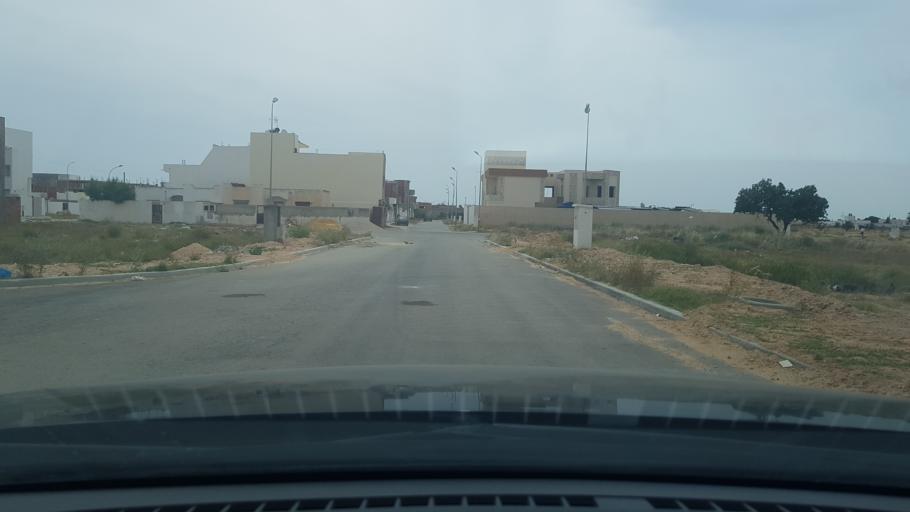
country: TN
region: Safaqis
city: Al Qarmadah
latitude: 34.8259
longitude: 10.7450
